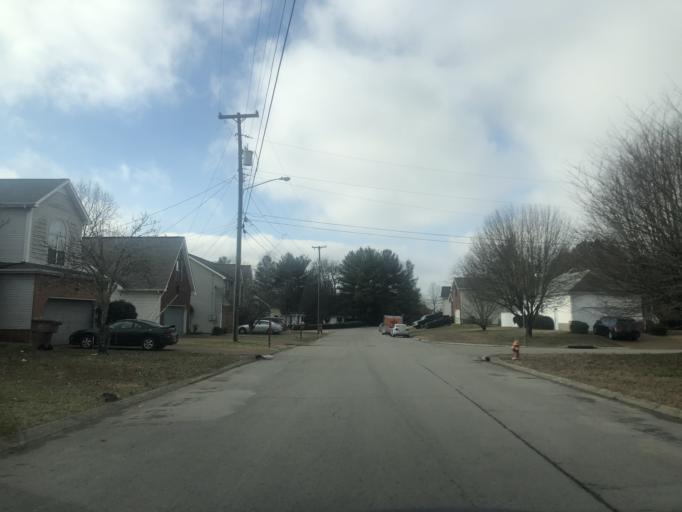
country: US
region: Tennessee
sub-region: Rutherford County
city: La Vergne
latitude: 36.0790
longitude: -86.6506
